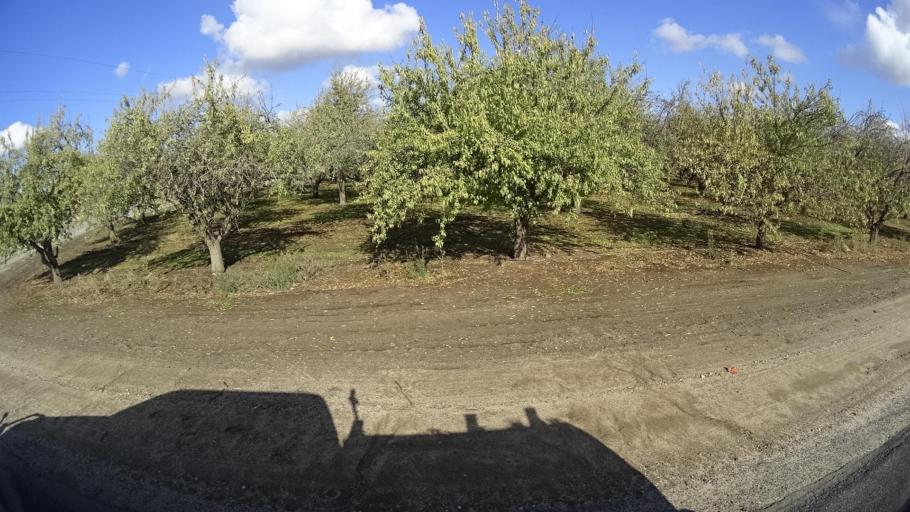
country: US
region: California
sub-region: Kern County
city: McFarland
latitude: 35.6454
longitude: -119.2406
